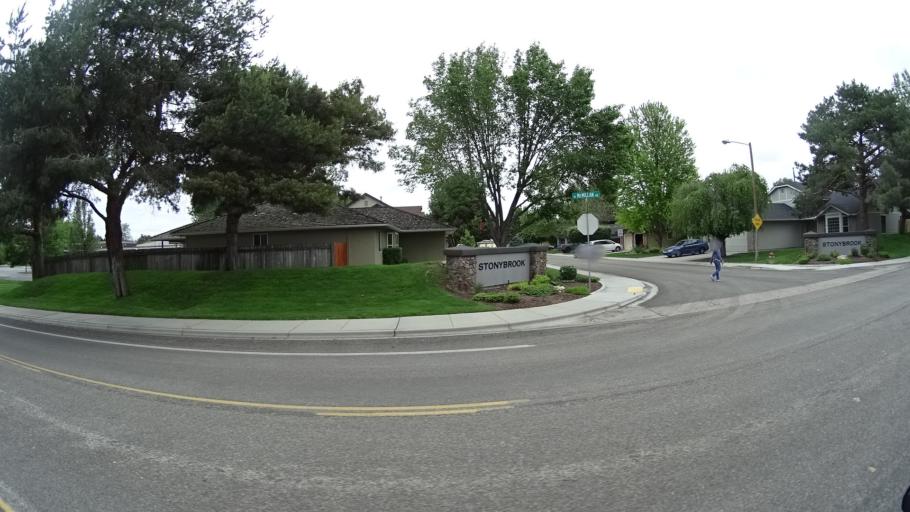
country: US
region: Idaho
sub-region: Ada County
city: Eagle
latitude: 43.6484
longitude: -116.3124
